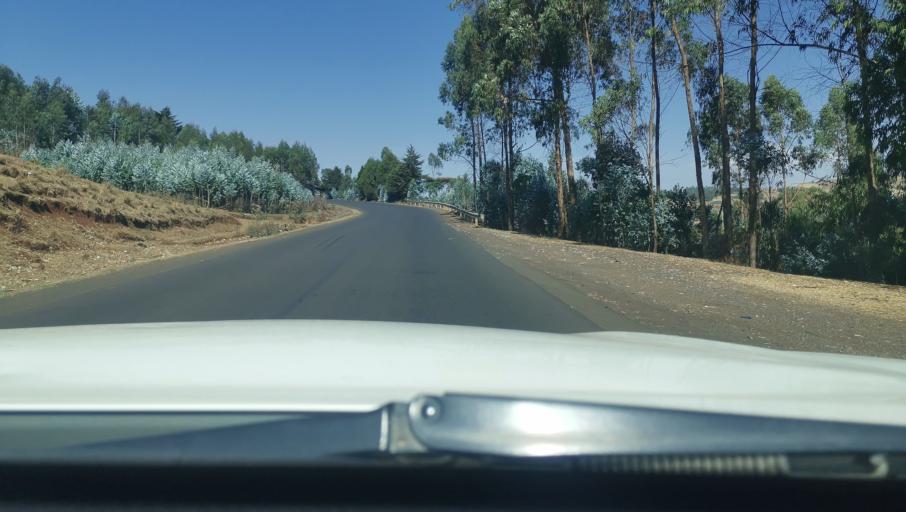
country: ET
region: Oromiya
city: Gedo
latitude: 8.9801
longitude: 37.4777
